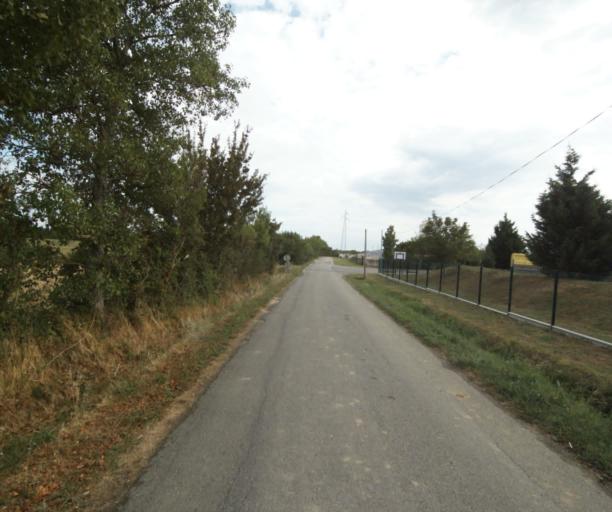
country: FR
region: Midi-Pyrenees
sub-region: Departement de la Haute-Garonne
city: Revel
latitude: 43.4537
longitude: 1.9710
